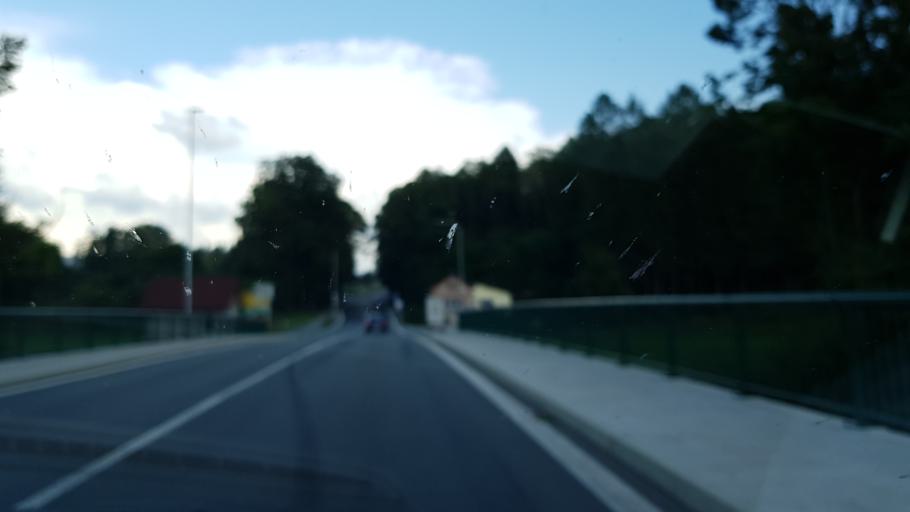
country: CZ
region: Pardubicky
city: Zamberk
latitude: 50.0942
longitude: 16.4448
